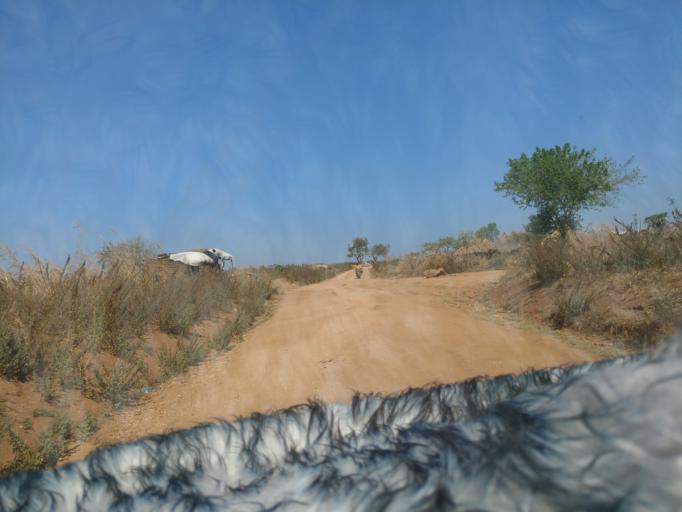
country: UG
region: Northern Region
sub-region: Yumbe District
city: Yumbe
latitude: 3.3926
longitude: 31.3222
